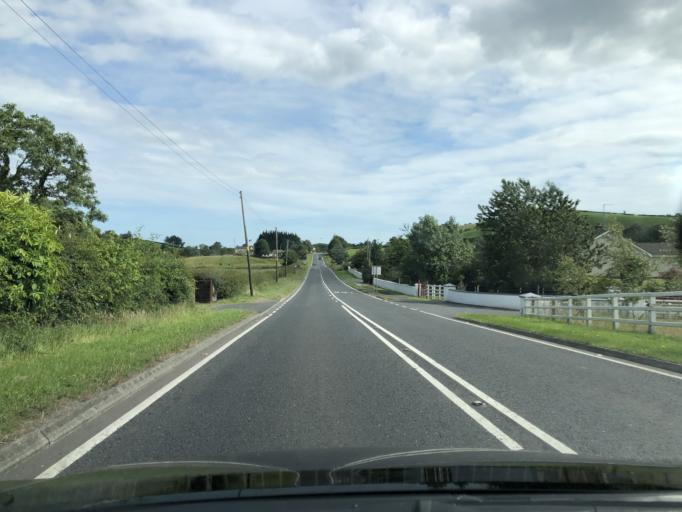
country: GB
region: Northern Ireland
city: Ballynahinch
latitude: 54.3829
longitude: -5.8773
